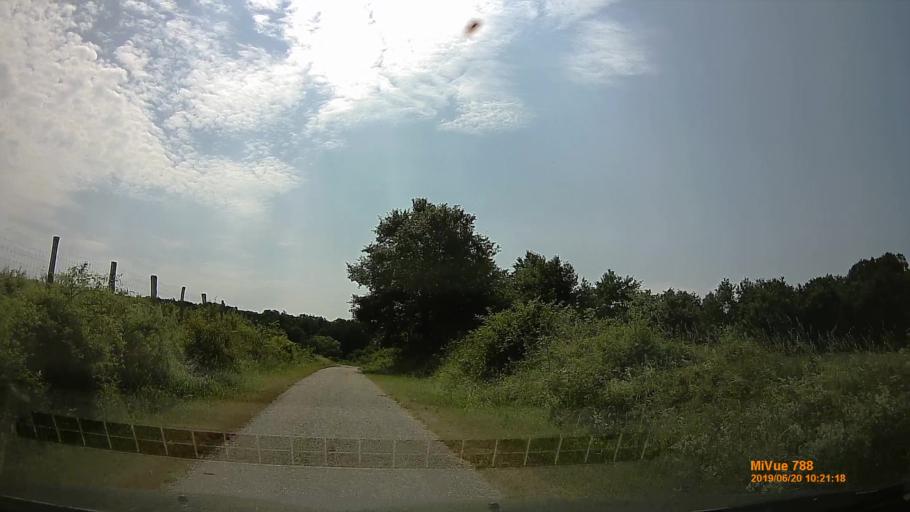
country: HU
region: Baranya
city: Mecseknadasd
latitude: 46.2097
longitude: 18.4755
